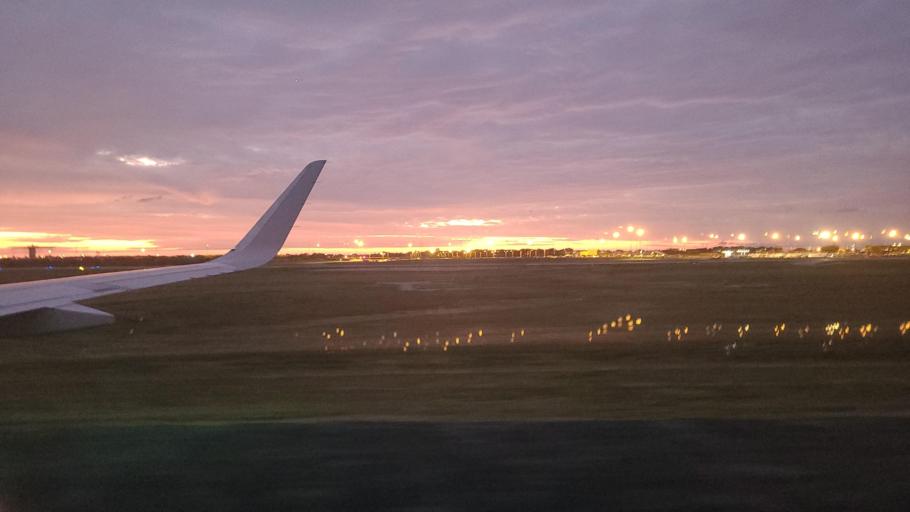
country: US
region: Texas
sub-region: Tarrant County
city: Euless
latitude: 32.8738
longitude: -97.0288
